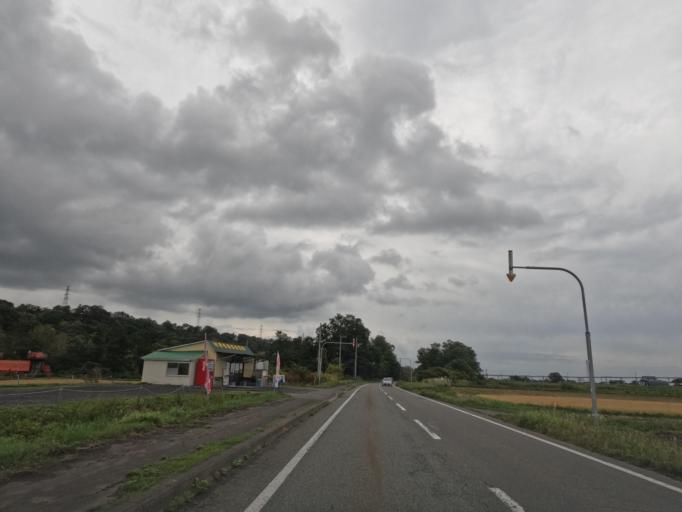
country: JP
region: Hokkaido
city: Date
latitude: 42.5126
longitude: 140.8634
